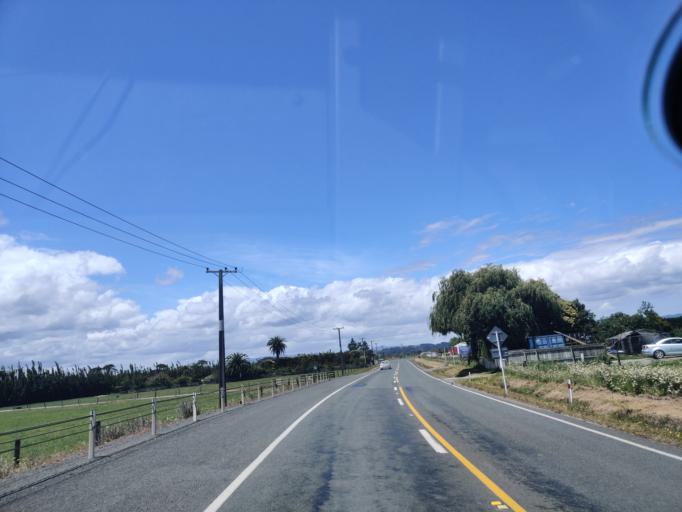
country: NZ
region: Northland
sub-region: Far North District
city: Kaitaia
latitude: -35.0284
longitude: 173.2526
